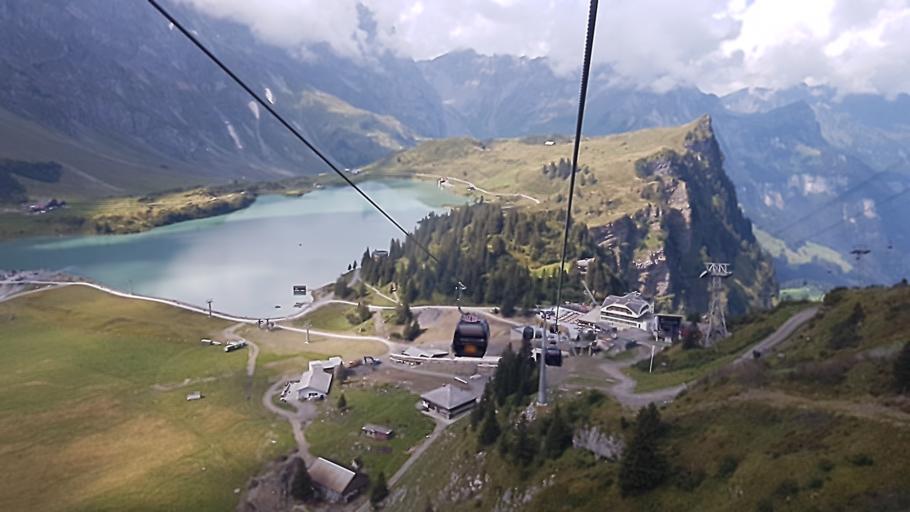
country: CH
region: Obwalden
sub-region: Obwalden
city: Engelberg
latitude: 46.7911
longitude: 8.4023
